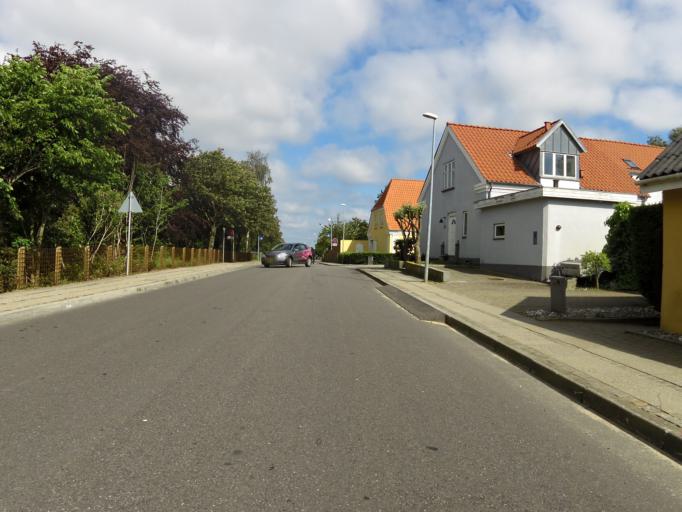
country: DK
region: South Denmark
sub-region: Esbjerg Kommune
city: Ribe
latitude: 55.3307
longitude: 8.7745
